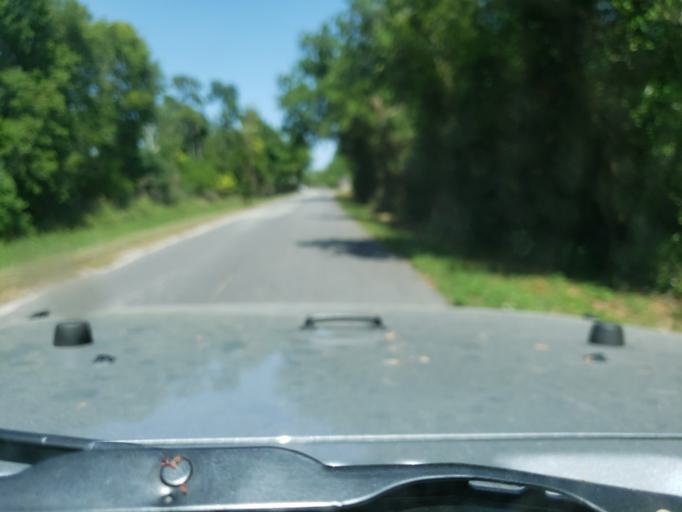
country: US
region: Georgia
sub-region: Chatham County
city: Thunderbolt
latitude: 32.0804
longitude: -81.0383
